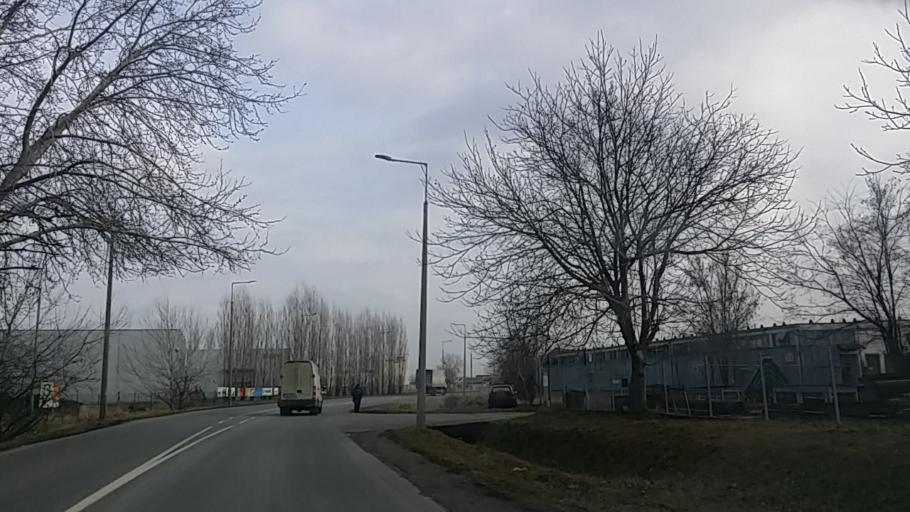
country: HU
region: Tolna
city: Szekszard
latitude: 46.3560
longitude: 18.7187
